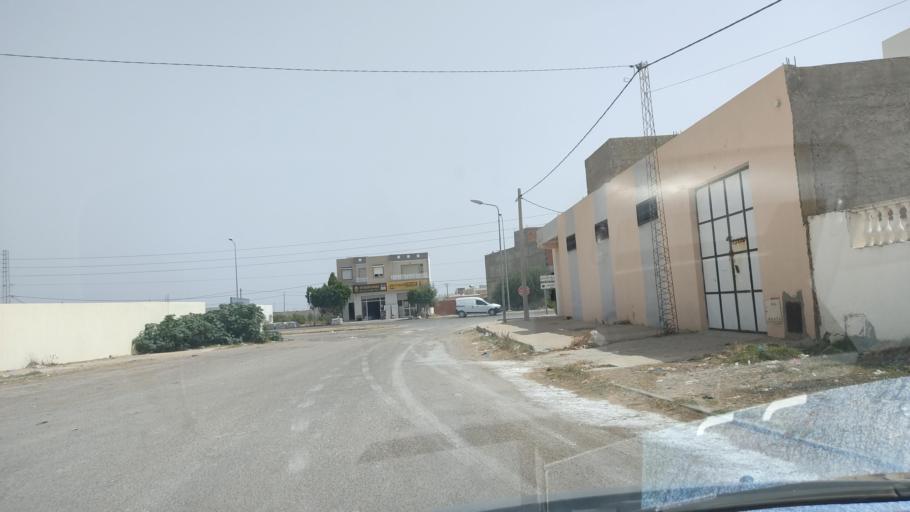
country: TN
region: Al Mahdiyah
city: El Jem
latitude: 35.1279
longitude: 10.7387
